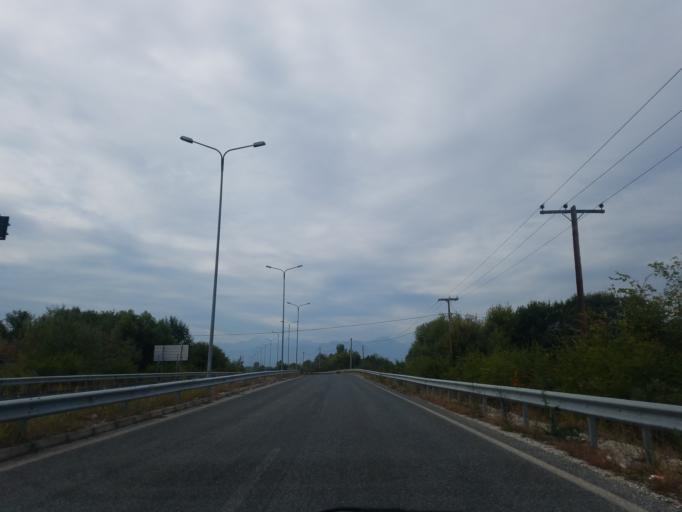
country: GR
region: Thessaly
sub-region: Trikala
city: Pyrgetos
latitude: 39.5711
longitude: 21.7422
